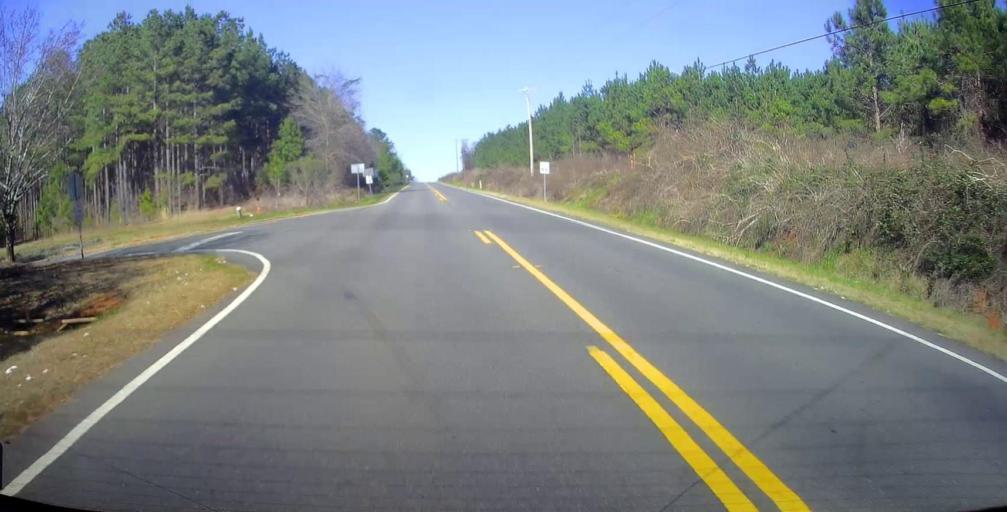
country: US
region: Georgia
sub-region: Macon County
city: Montezuma
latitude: 32.3234
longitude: -84.0226
